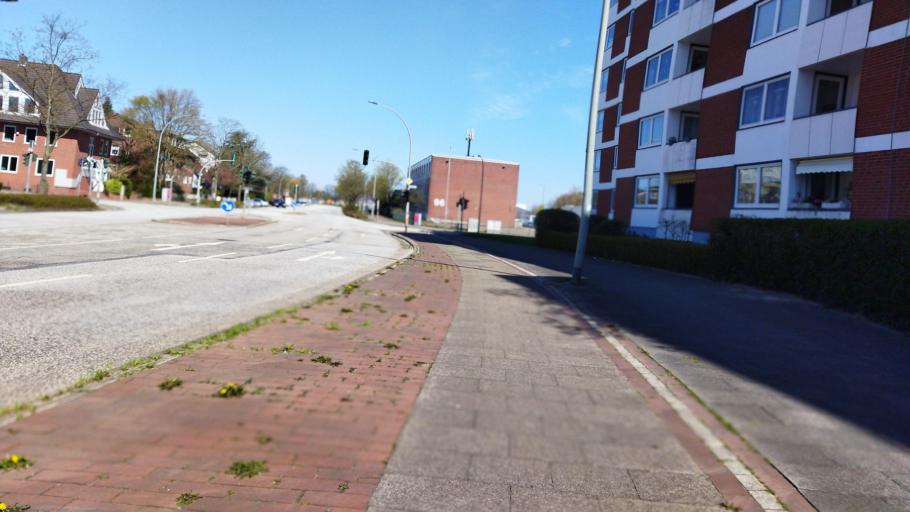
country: DE
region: Bremen
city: Bremerhaven
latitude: 53.5425
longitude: 8.5956
